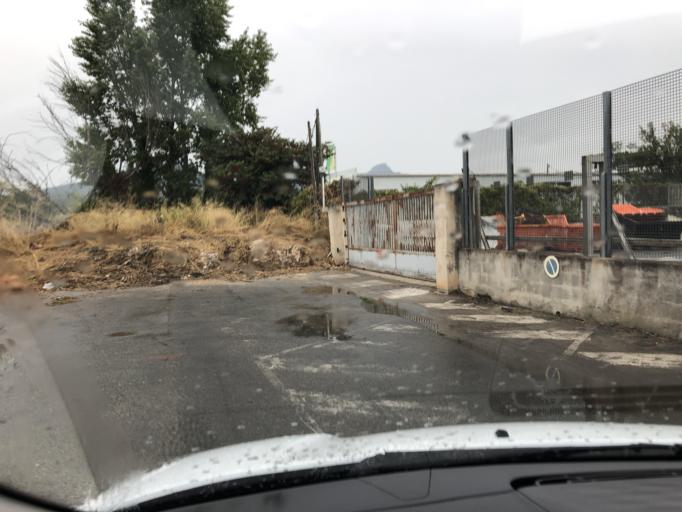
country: FR
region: Provence-Alpes-Cote d'Azur
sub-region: Departement des Bouches-du-Rhone
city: La Penne-sur-Huveaune
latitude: 43.2850
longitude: 5.5329
